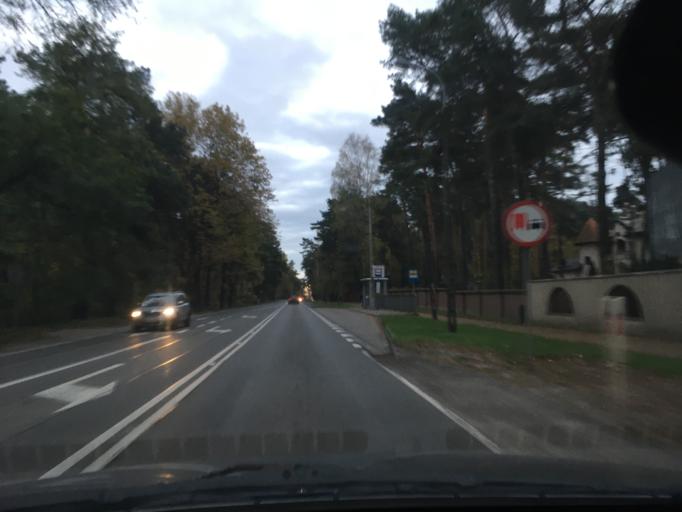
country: PL
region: Masovian Voivodeship
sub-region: Powiat piaseczynski
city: Lesznowola
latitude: 52.0981
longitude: 20.9103
